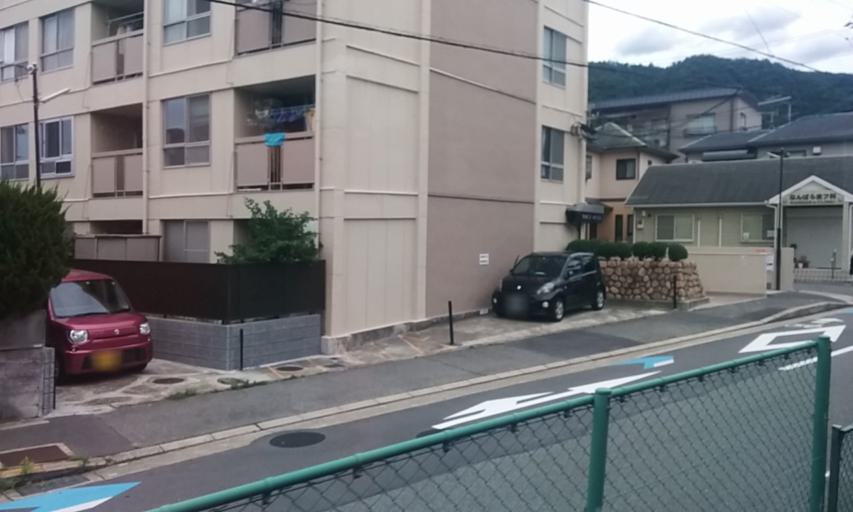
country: JP
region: Osaka
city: Mino
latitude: 34.8320
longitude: 135.4679
